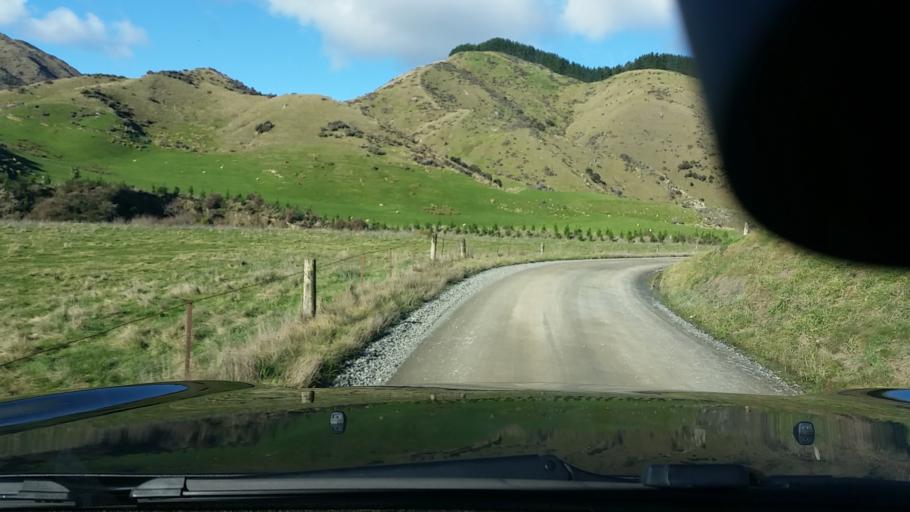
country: NZ
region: Marlborough
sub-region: Marlborough District
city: Blenheim
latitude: -41.6036
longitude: 173.9730
